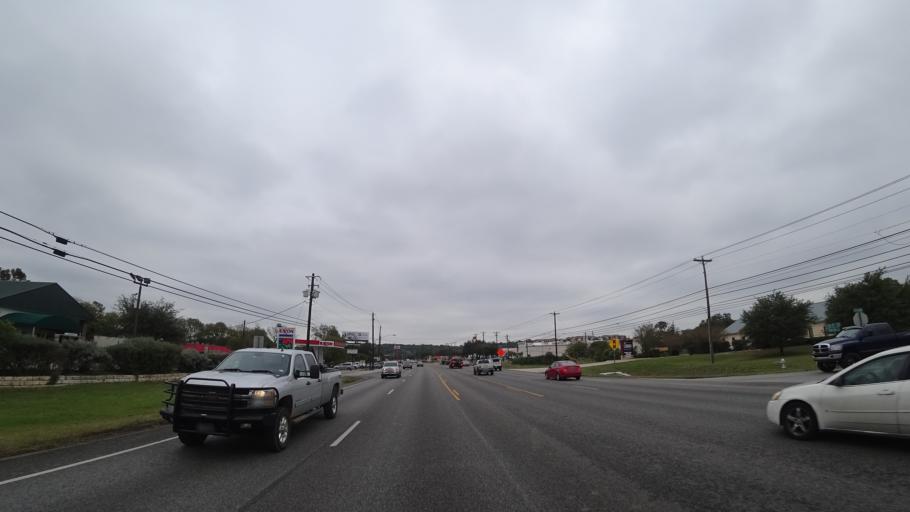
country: US
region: Texas
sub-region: Travis County
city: Barton Creek
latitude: 30.2372
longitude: -97.8783
